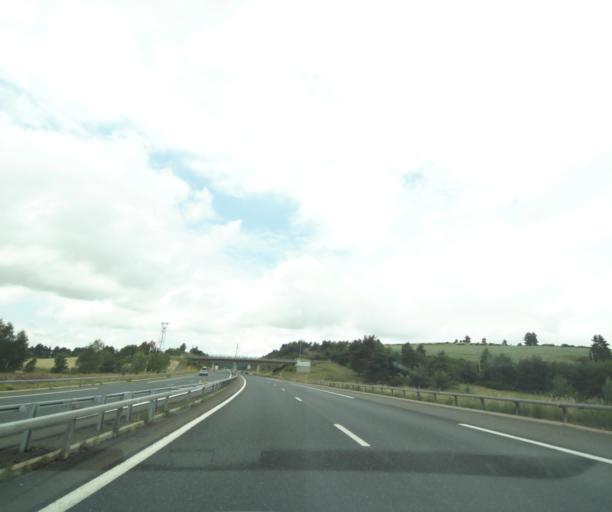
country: FR
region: Languedoc-Roussillon
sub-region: Departement de la Lozere
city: Aumont-Aubrac
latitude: 44.7521
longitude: 3.2893
